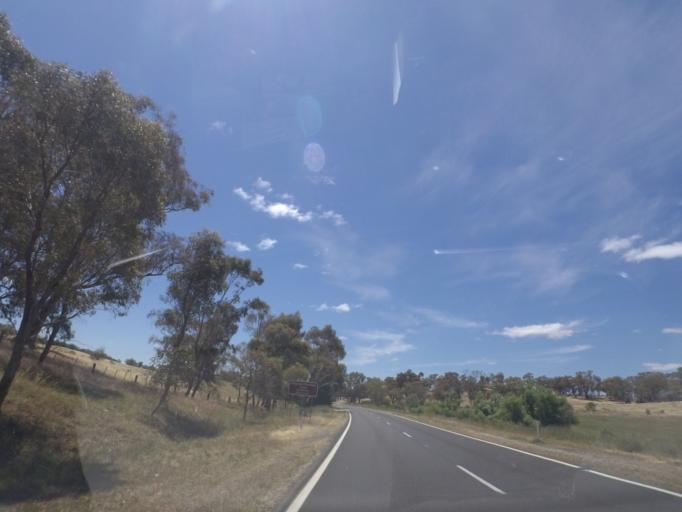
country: AU
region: Victoria
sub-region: Mount Alexander
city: Castlemaine
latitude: -37.1593
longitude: 144.1590
